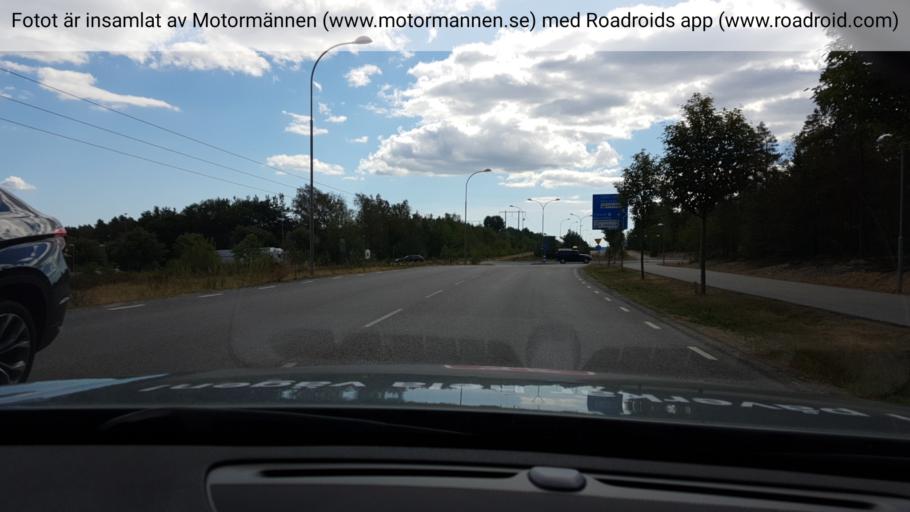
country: SE
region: Stockholm
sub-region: Nacka Kommun
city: Alta
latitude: 59.2437
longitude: 18.1956
